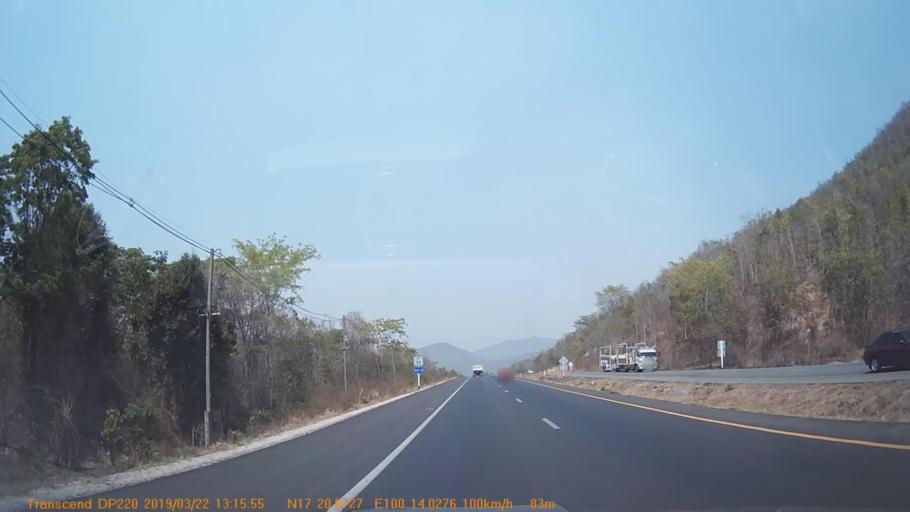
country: TH
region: Uttaradit
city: Phichai
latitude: 17.3449
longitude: 100.2339
